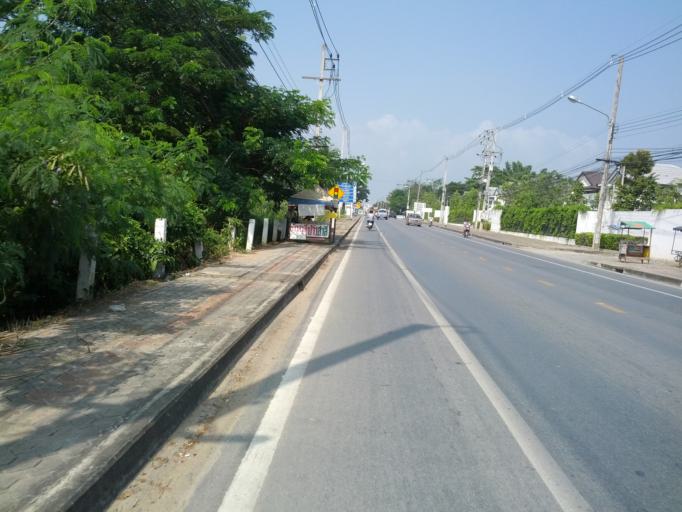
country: TH
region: Chiang Mai
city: Chiang Mai
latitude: 18.7791
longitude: 99.0478
